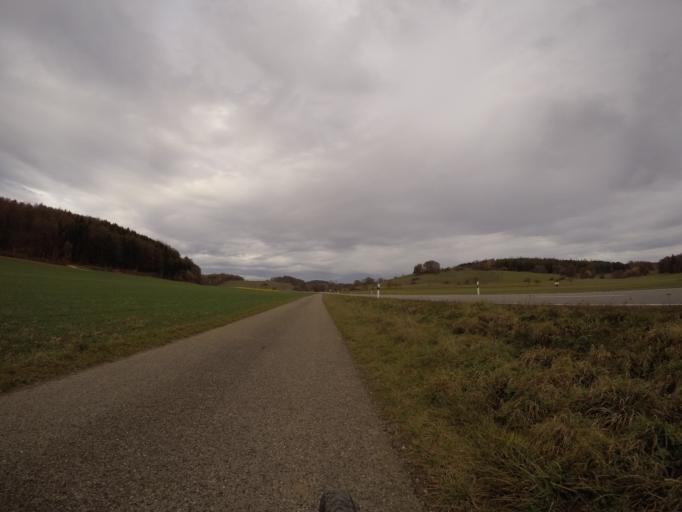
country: DE
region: Baden-Wuerttemberg
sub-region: Tuebingen Region
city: Sankt Johann
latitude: 48.4137
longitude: 9.2865
